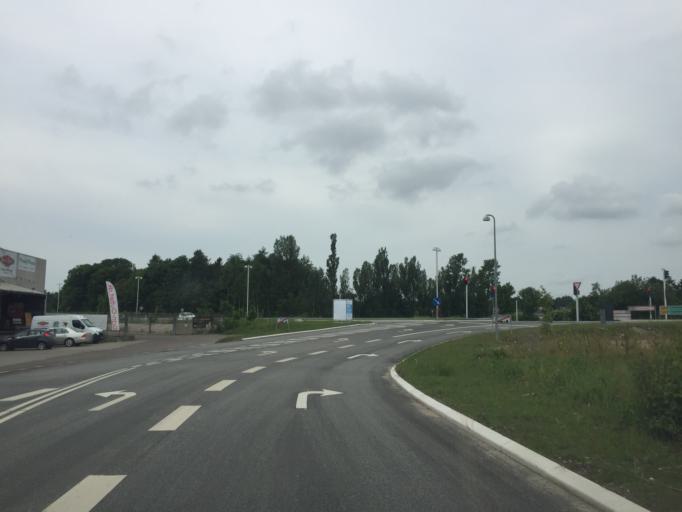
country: DK
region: Capital Region
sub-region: Fureso Kommune
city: Farum
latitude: 55.8222
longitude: 12.3688
